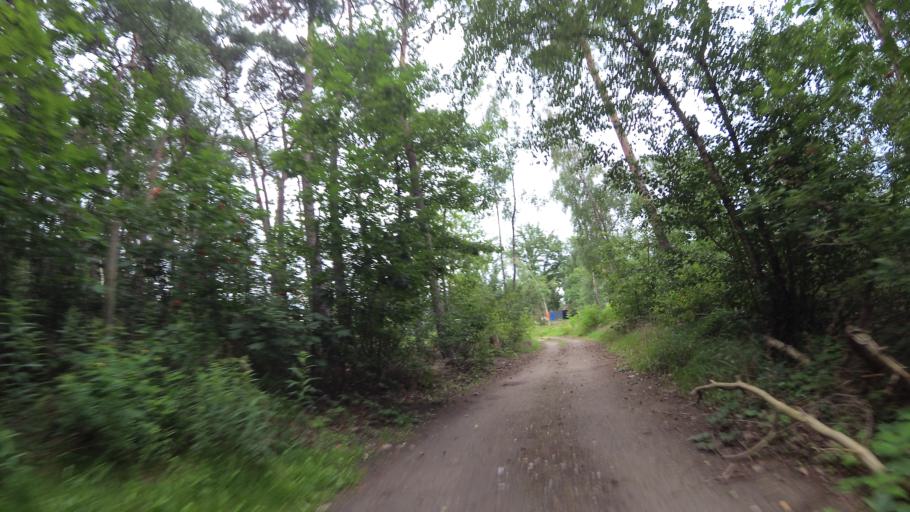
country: NL
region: North Brabant
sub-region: Gemeente Breda
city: Hoge Vucht
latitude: 51.6372
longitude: 4.7990
